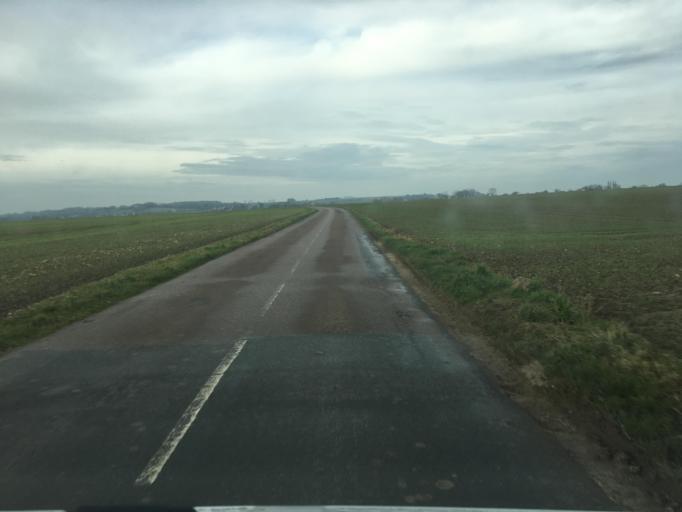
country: FR
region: Lower Normandy
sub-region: Departement du Calvados
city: Ver-sur-Mer
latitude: 49.3279
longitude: -0.5744
